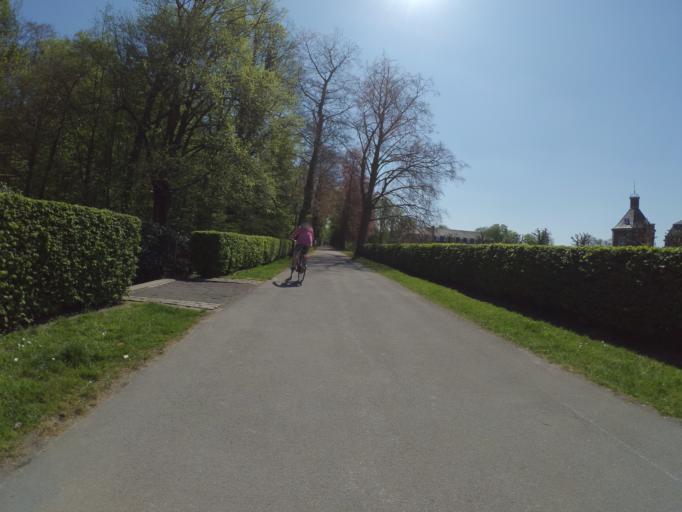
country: DE
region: North Rhine-Westphalia
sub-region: Regierungsbezirk Munster
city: Nordkirchen
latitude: 51.7321
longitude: 7.5362
